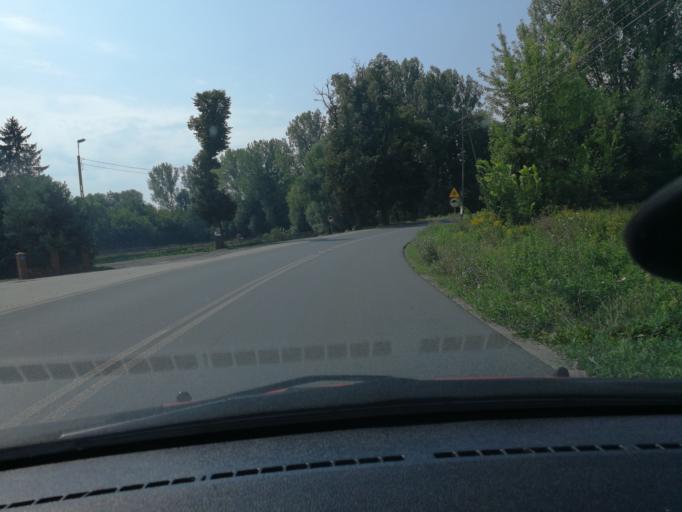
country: PL
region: Lodz Voivodeship
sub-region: powiat Lowicki
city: Bobrowniki
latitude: 52.0218
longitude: 20.0551
